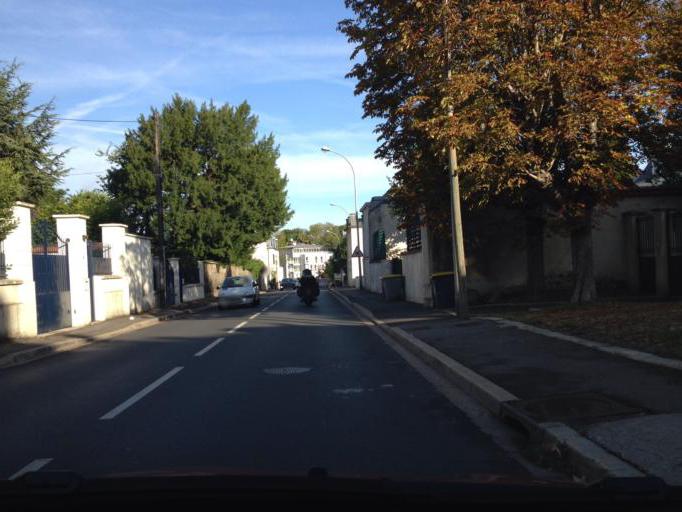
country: FR
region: Ile-de-France
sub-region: Departement des Hauts-de-Seine
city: Sevres
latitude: 48.8221
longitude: 2.2264
